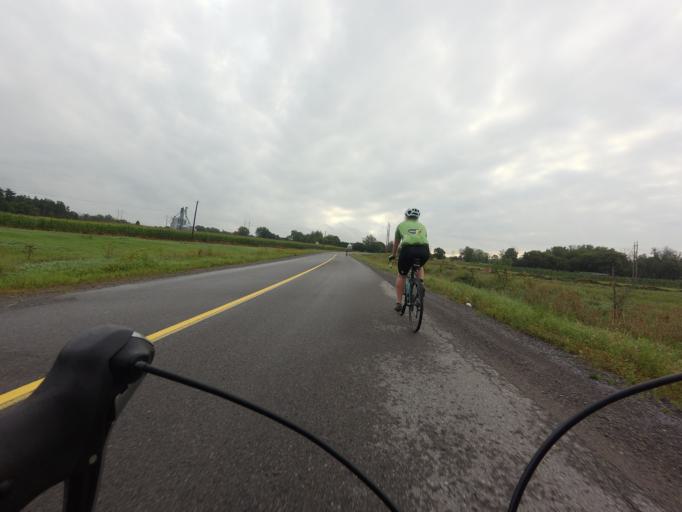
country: CA
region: Ontario
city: Bells Corners
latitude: 45.2634
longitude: -75.8151
